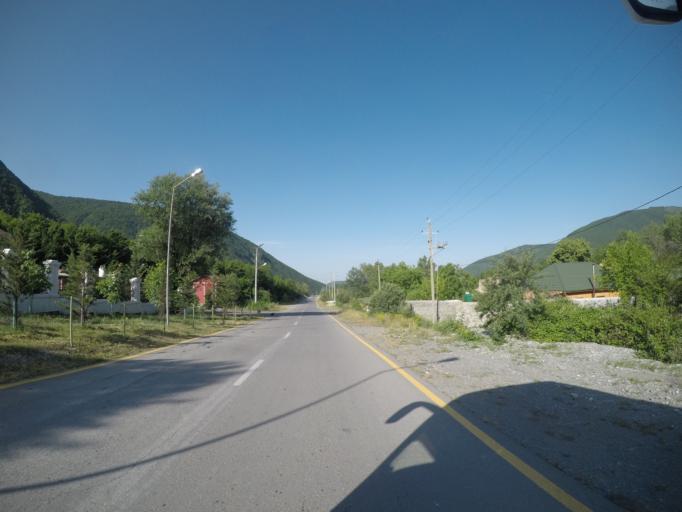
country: AZ
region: Shaki City
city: Sheki
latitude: 41.2528
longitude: 47.2078
